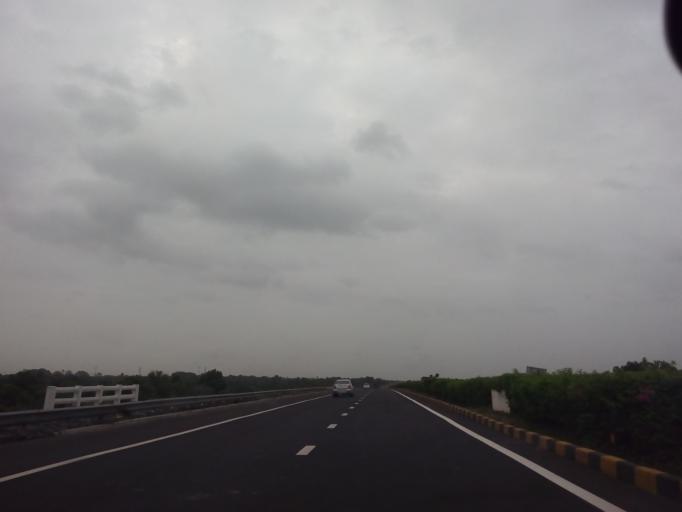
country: IN
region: Gujarat
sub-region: Kheda
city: Nadiad
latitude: 22.7234
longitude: 72.8760
